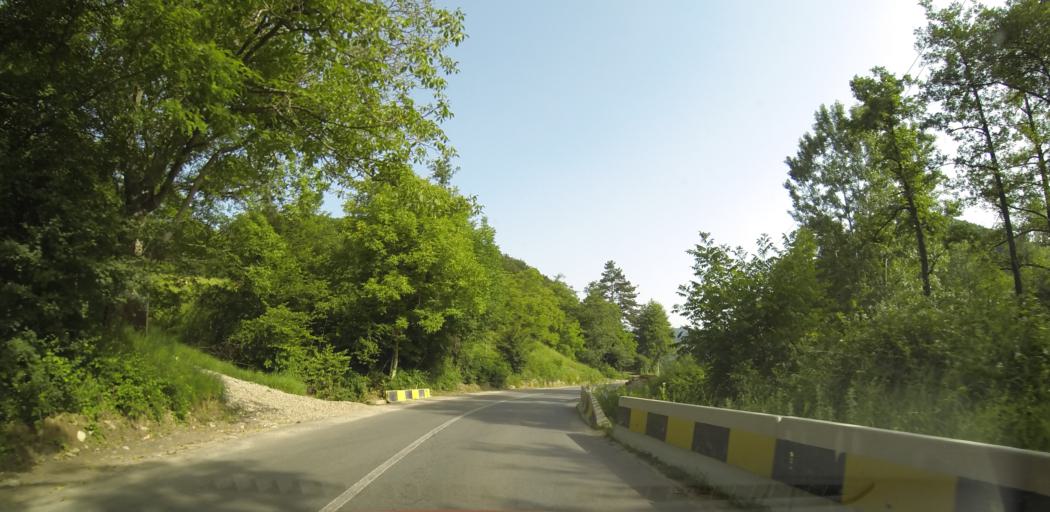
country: RO
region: Valcea
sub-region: Oras Baile Olanesti
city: Olanesti
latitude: 45.1868
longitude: 24.2530
